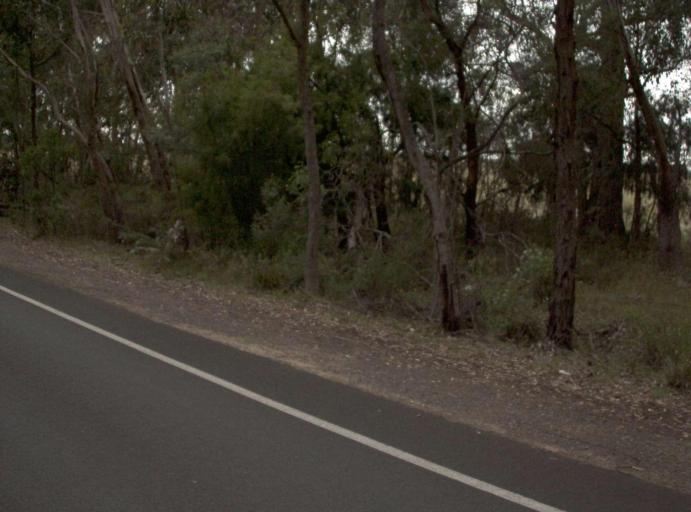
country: AU
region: Victoria
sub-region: Wellington
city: Sale
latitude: -38.4104
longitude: 146.9639
